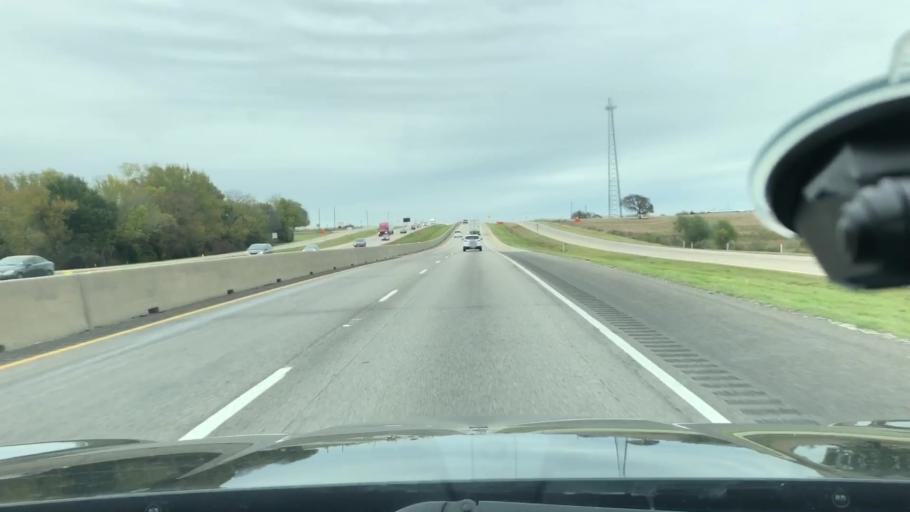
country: US
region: Texas
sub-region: Hunt County
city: Commerce
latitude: 33.1314
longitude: -95.8056
